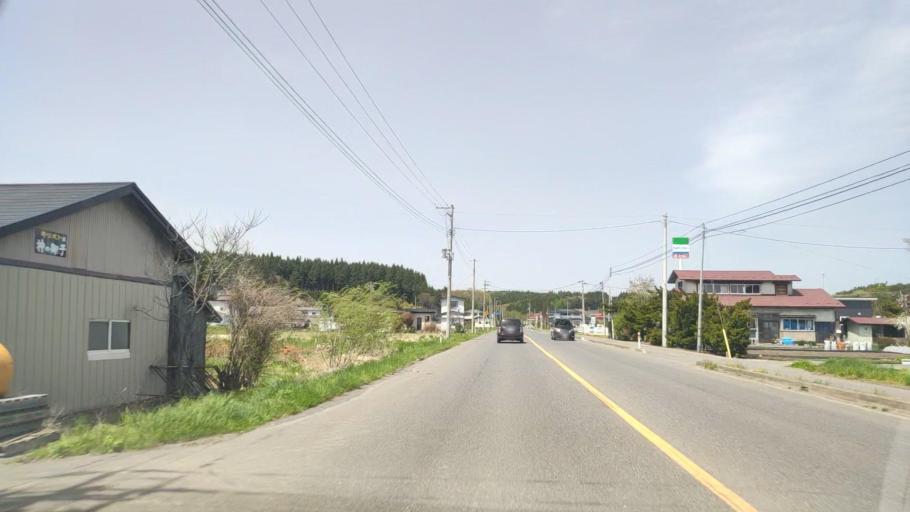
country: JP
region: Aomori
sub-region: Misawa Shi
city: Inuotose
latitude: 40.5586
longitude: 141.3867
